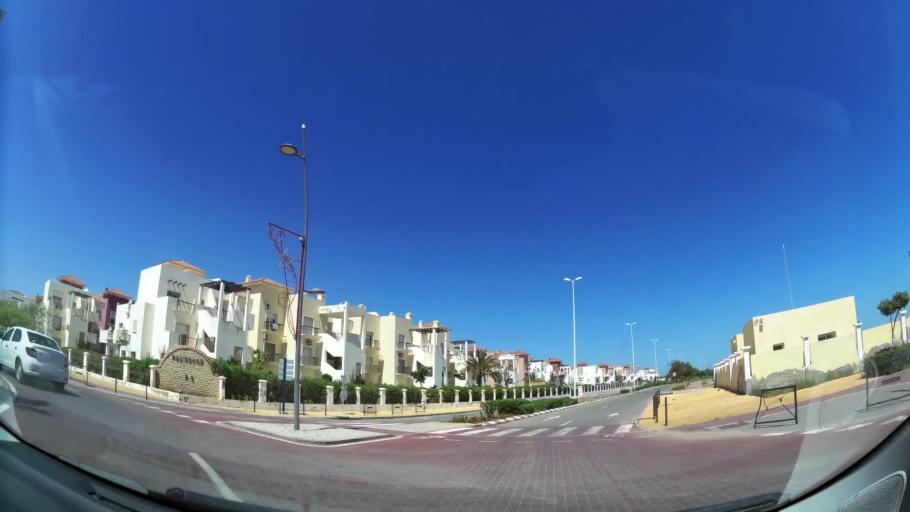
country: MA
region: Oriental
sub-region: Berkane-Taourirt
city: Madagh
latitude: 35.1000
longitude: -2.3000
